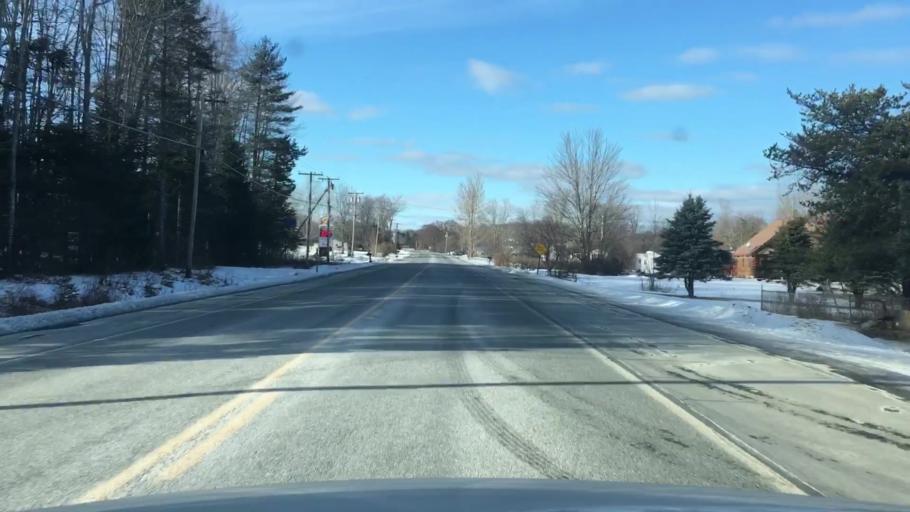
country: US
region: Maine
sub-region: Penobscot County
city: Eddington
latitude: 44.8227
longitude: -68.6507
